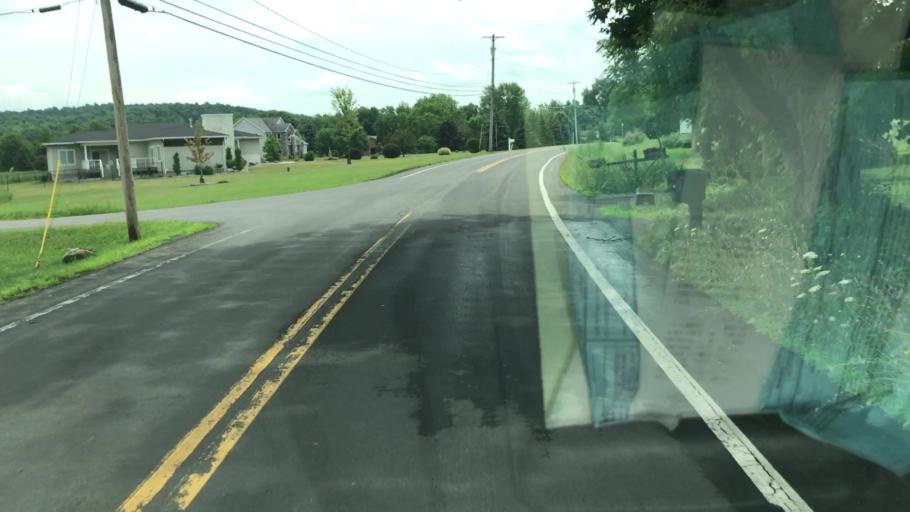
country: US
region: New York
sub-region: Onondaga County
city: Manlius
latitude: 42.9692
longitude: -75.9875
